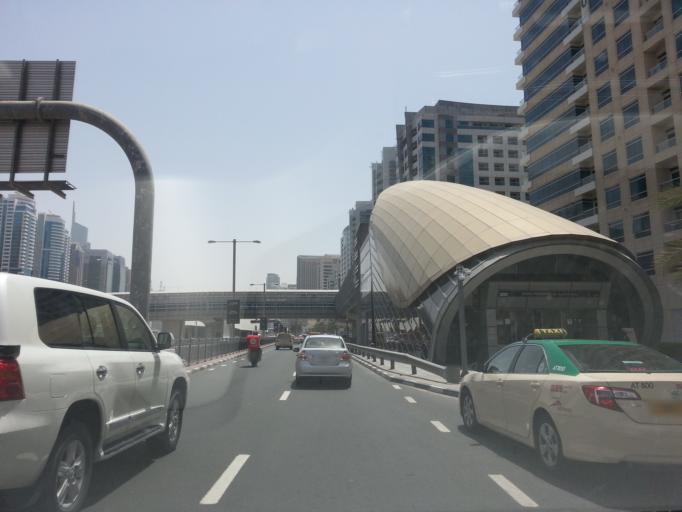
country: AE
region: Dubai
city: Dubai
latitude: 25.0823
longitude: 55.1482
